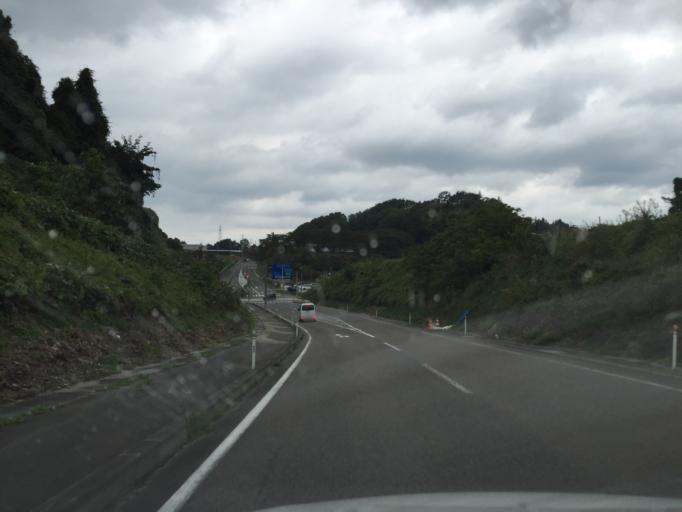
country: JP
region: Fukushima
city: Miharu
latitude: 37.4421
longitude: 140.5107
